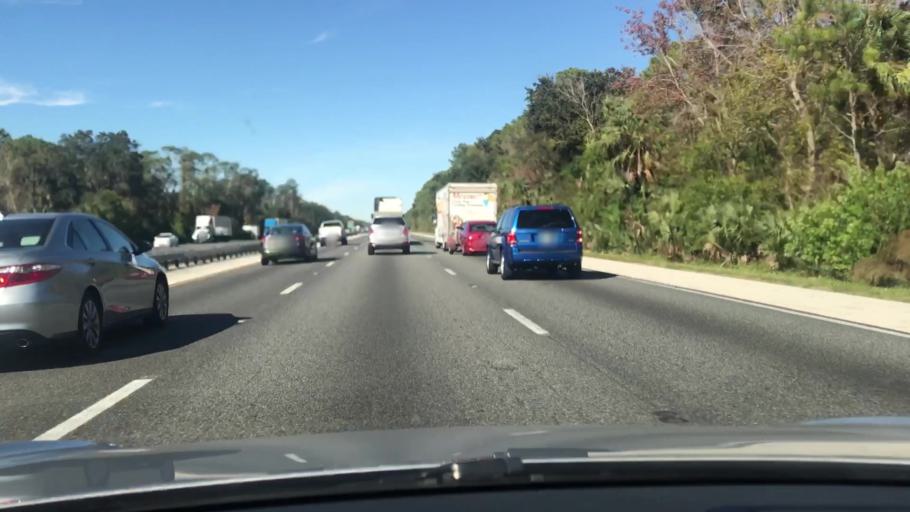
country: US
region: Florida
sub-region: Volusia County
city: Ormond-by-the-Sea
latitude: 29.3751
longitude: -81.1426
